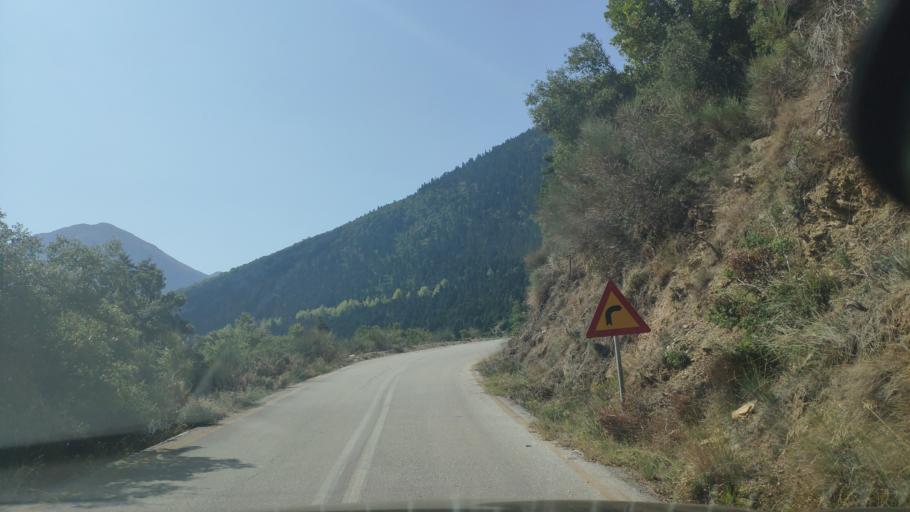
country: GR
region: Peloponnese
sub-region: Nomos Korinthias
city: Nemea
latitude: 37.8595
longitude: 22.3845
